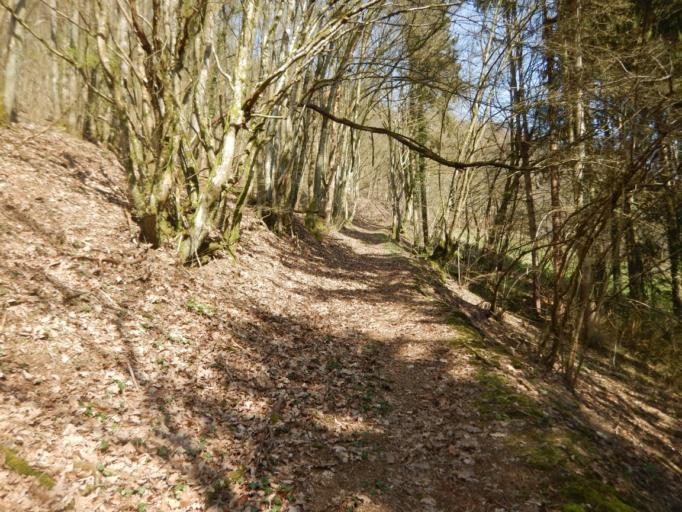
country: LU
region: Diekirch
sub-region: Canton de Diekirch
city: Bourscheid
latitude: 49.9352
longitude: 6.0701
